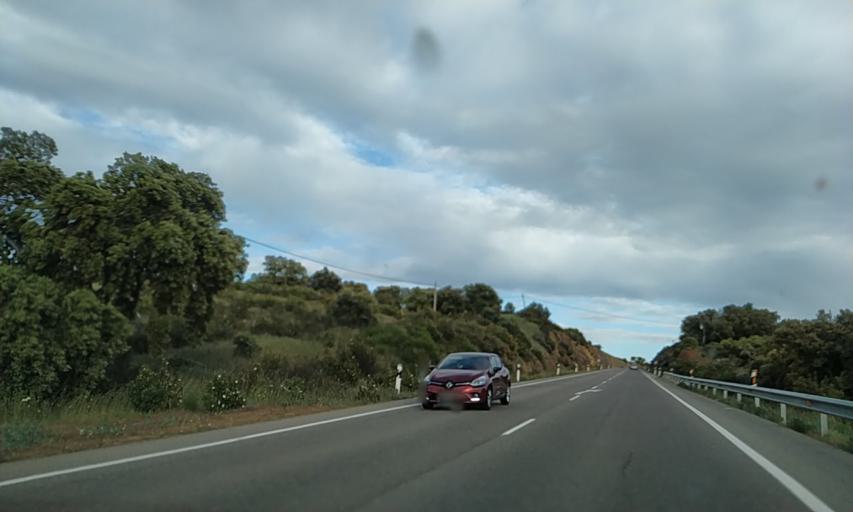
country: ES
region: Extremadura
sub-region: Provincia de Caceres
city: Pedroso de Acim
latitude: 39.8272
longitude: -6.3779
